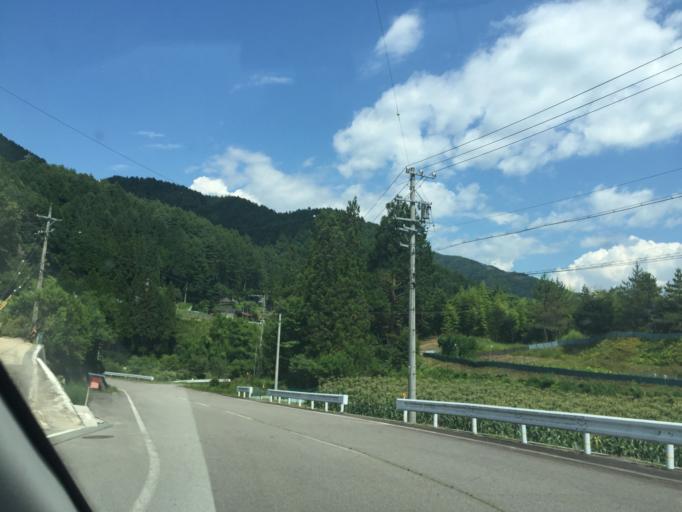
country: JP
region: Nagano
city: Iida
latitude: 35.3693
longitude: 137.7029
